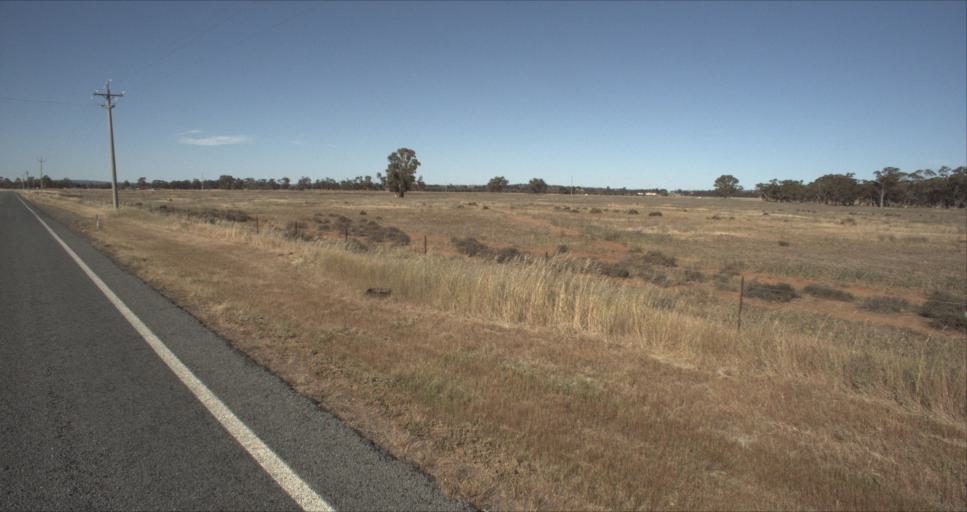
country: AU
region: New South Wales
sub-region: Leeton
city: Leeton
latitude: -34.6177
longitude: 146.3996
